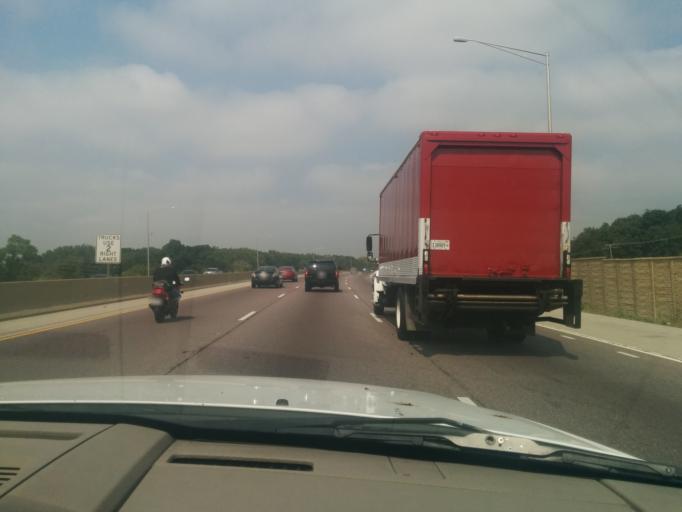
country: US
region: Illinois
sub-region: DuPage County
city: Addison
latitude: 41.9297
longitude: -87.9744
